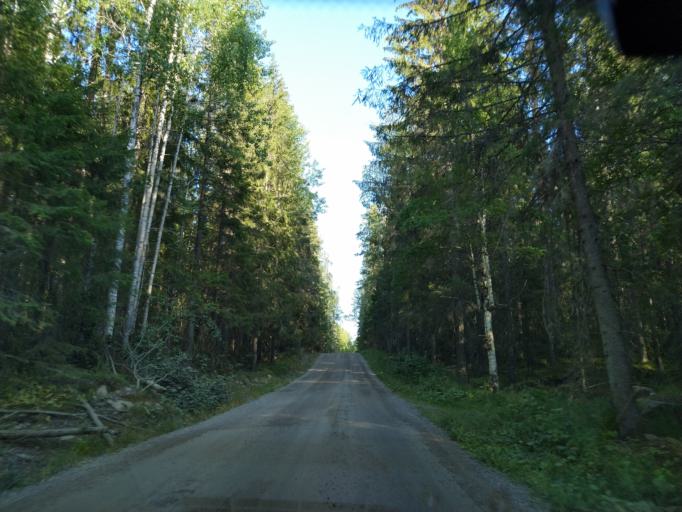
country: FI
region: Central Finland
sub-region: Jaemsae
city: Kuhmoinen
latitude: 61.6790
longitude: 24.9866
